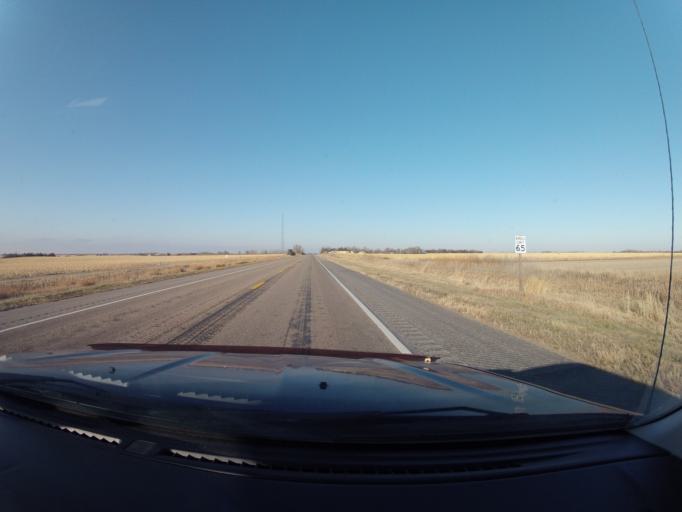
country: US
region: Nebraska
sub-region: Kearney County
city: Minden
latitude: 40.5697
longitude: -98.9518
